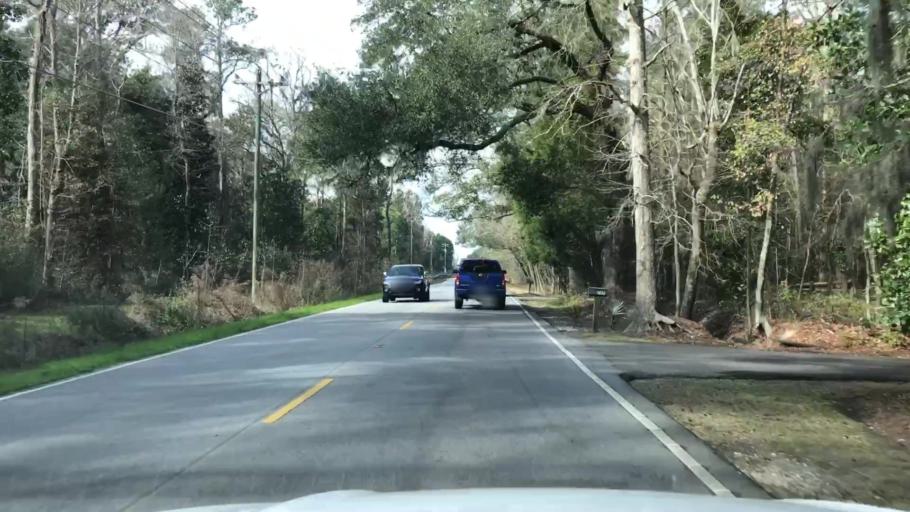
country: US
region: South Carolina
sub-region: Charleston County
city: Shell Point
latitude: 32.7753
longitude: -80.0882
